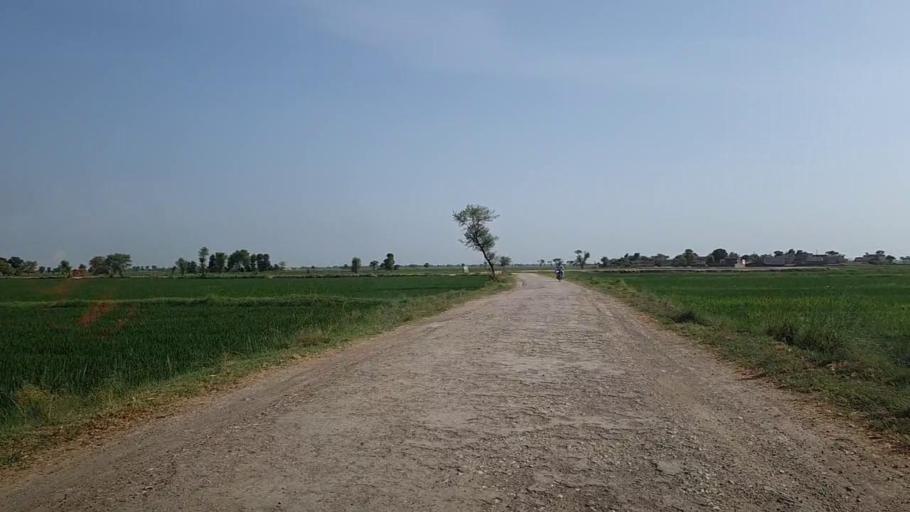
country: PK
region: Sindh
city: Mehar
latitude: 27.1105
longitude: 67.8472
